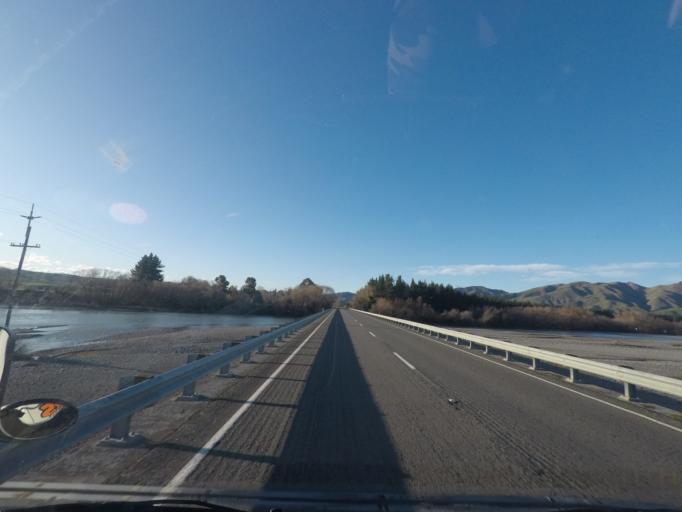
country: NZ
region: Canterbury
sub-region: Kaikoura District
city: Kaikoura
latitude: -42.7214
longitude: 173.2843
